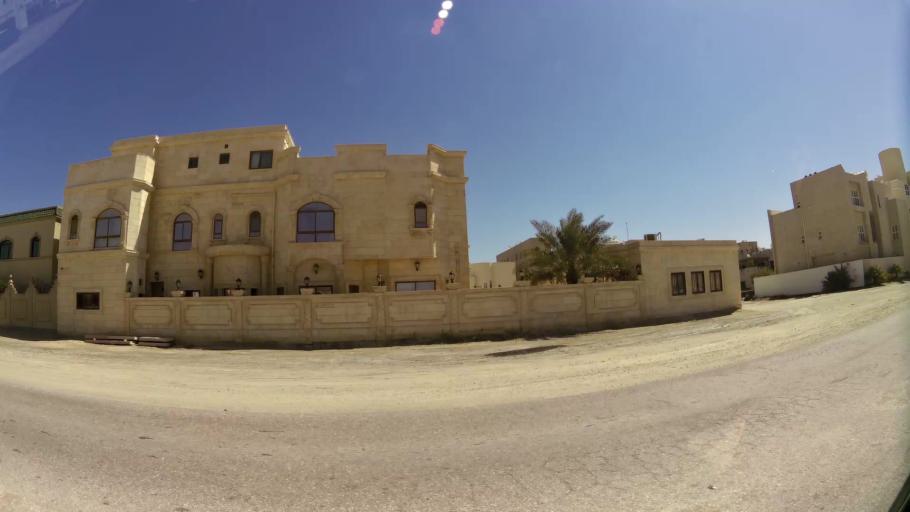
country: BH
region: Muharraq
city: Al Muharraq
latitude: 26.2748
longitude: 50.6027
